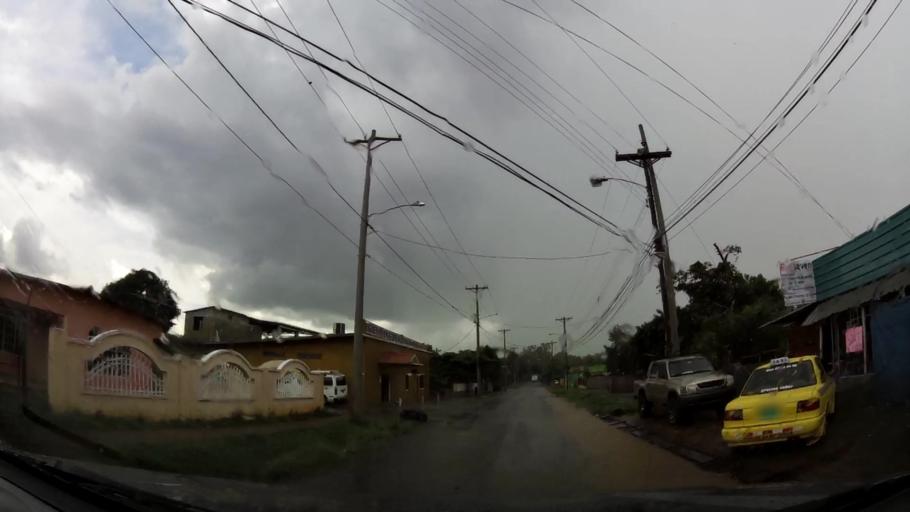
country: PA
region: Panama
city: Cabra Numero Uno
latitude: 9.1042
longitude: -79.3323
